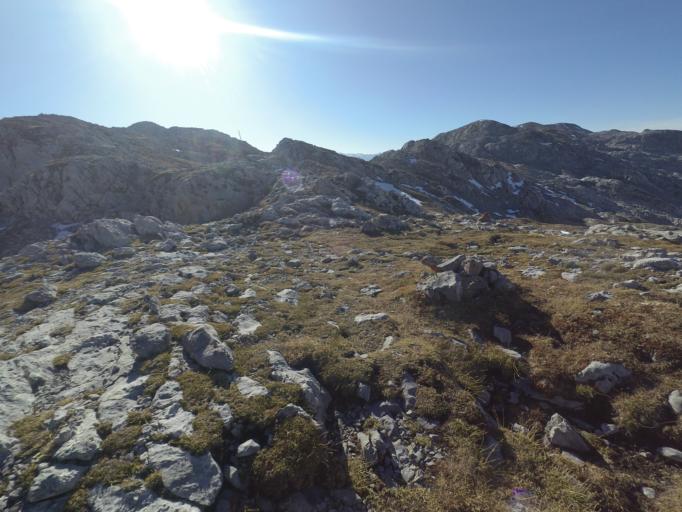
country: AT
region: Salzburg
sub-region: Politischer Bezirk Sankt Johann im Pongau
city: Werfenweng
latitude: 47.5011
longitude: 13.2435
